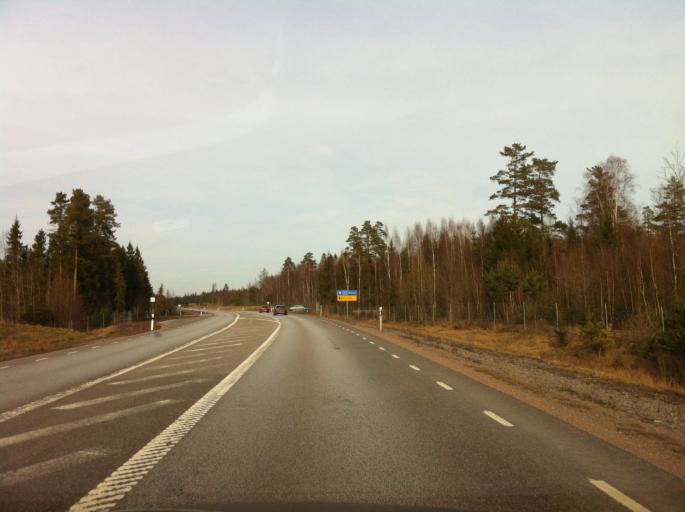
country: SE
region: Vaestra Goetaland
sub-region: Gullspangs Kommun
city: Gullspang
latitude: 58.8591
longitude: 14.0049
